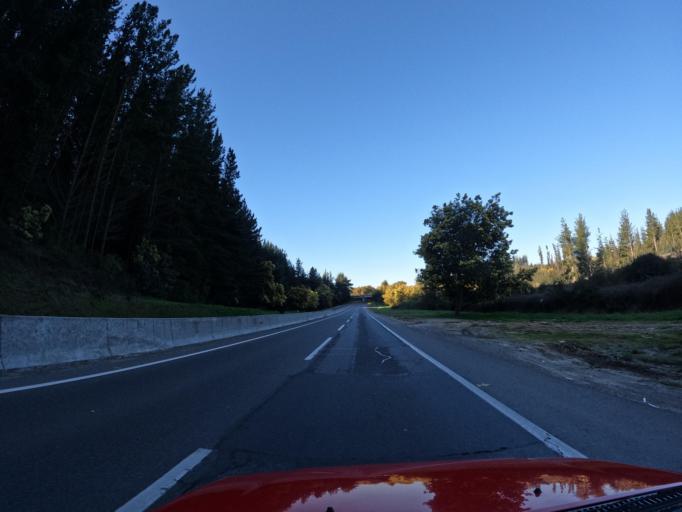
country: CL
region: Biobio
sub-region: Provincia de Concepcion
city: Penco
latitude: -36.7277
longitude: -72.8402
